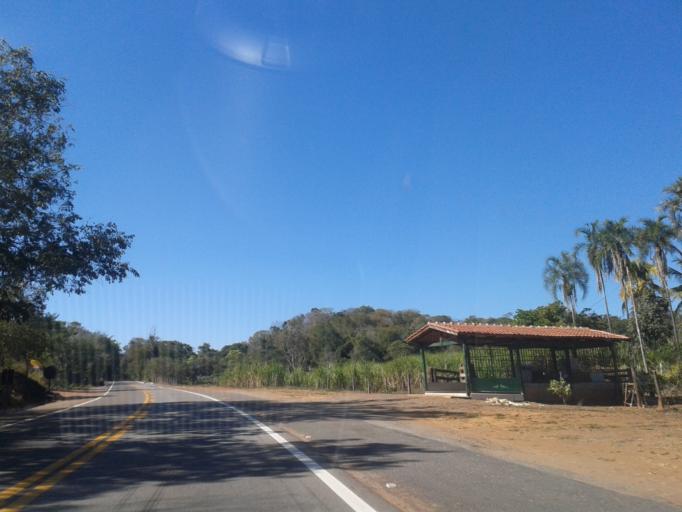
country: BR
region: Goias
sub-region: Goias
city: Goias
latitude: -15.8995
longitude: -50.1103
